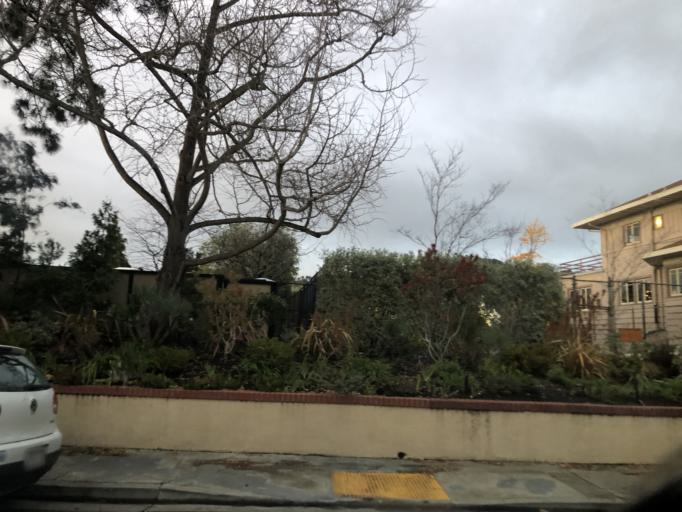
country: US
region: California
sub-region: Alameda County
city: Piedmont
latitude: 37.8528
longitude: -122.2463
